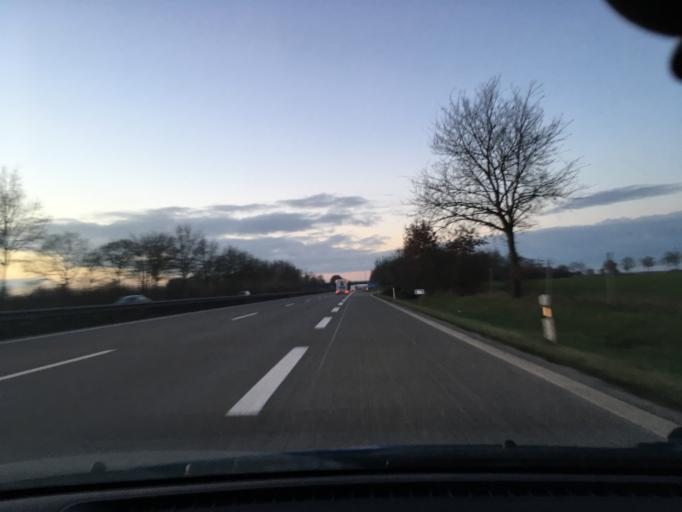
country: DE
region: Schleswig-Holstein
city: Hohenfelde
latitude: 53.8407
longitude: 9.6063
